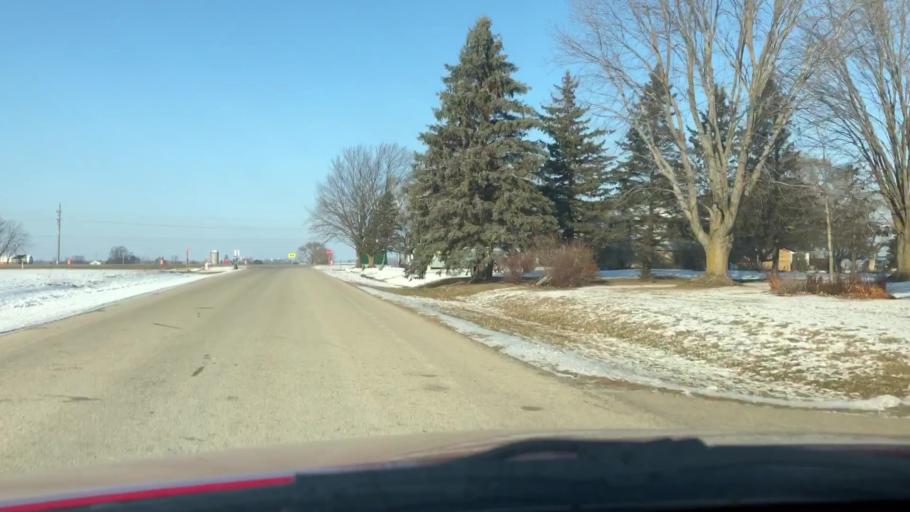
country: US
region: Wisconsin
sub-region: Outagamie County
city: Seymour
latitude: 44.4990
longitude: -88.3089
